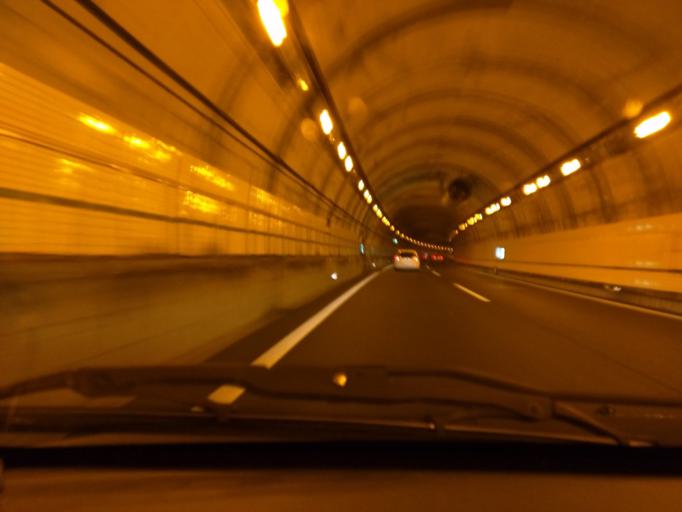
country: JP
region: Niigata
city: Kashiwazaki
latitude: 37.3199
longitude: 138.4557
